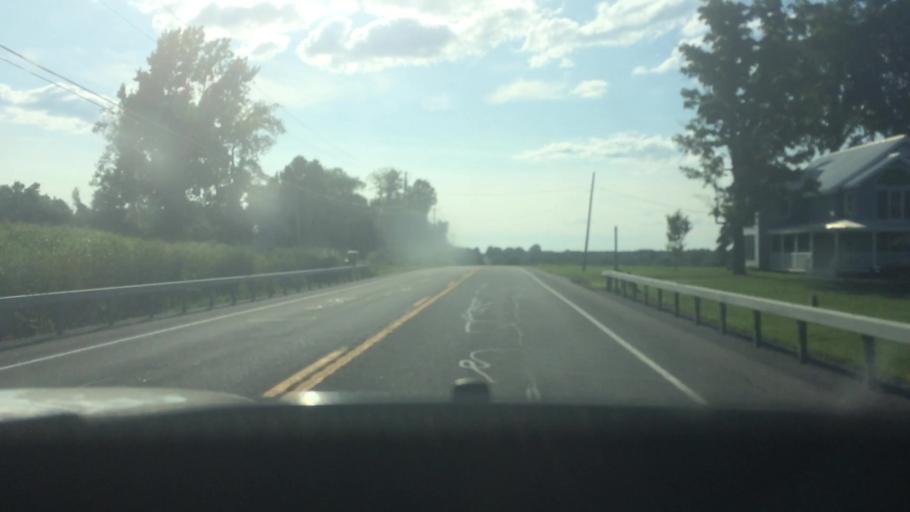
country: US
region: New York
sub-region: St. Lawrence County
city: Potsdam
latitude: 44.6892
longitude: -74.7264
